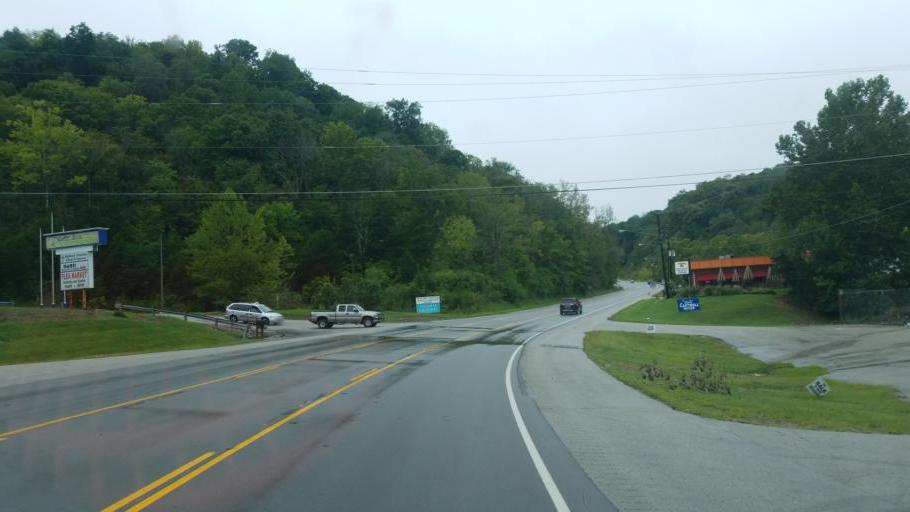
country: US
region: Kentucky
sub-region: Mason County
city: Maysville
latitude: 38.6385
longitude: -83.7590
